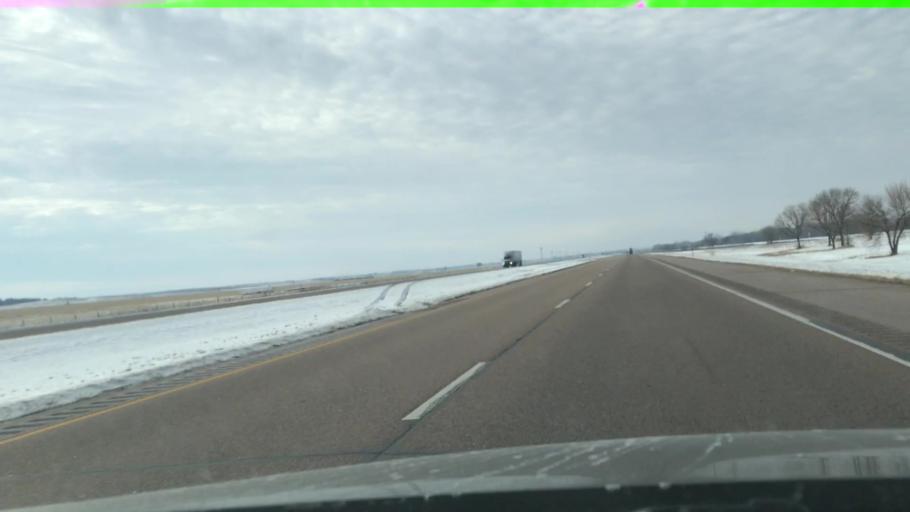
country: US
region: Nebraska
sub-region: Keith County
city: Ogallala
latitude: 41.1189
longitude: -101.6026
